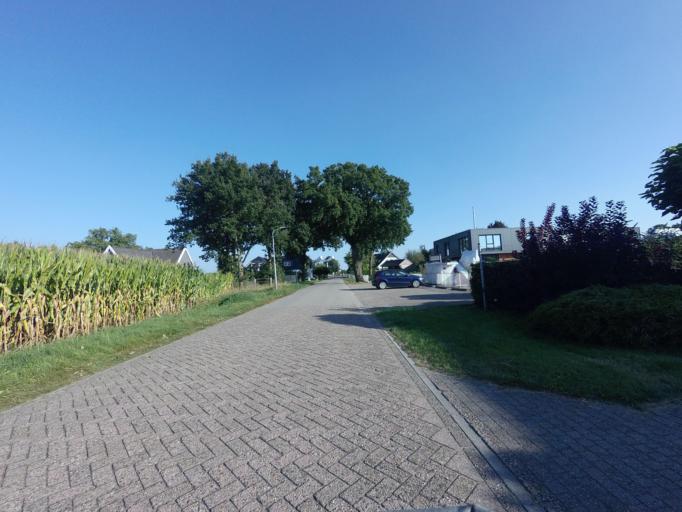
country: NL
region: Overijssel
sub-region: Gemeente Hardenberg
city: Hardenberg
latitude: 52.5603
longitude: 6.6392
